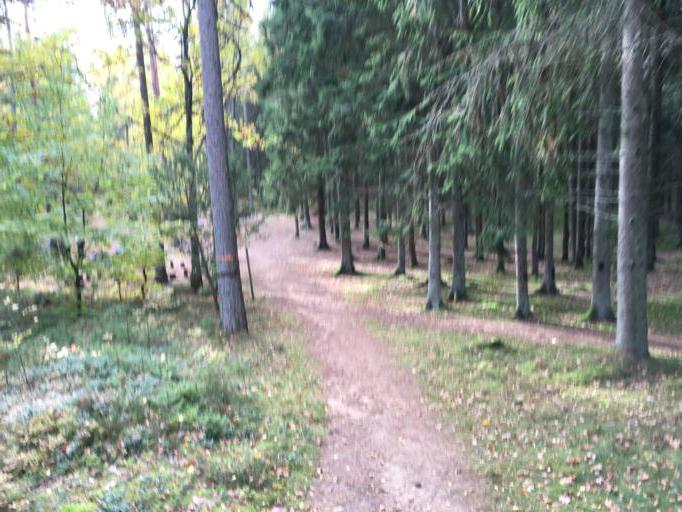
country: SE
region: Skane
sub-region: Hassleholms Kommun
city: Bjarnum
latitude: 56.2120
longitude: 13.6411
